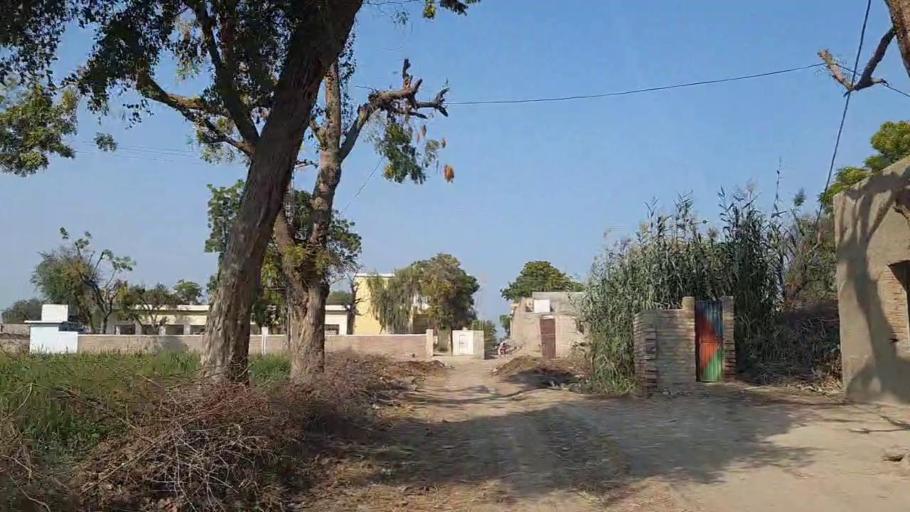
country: PK
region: Sindh
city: Moro
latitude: 26.6848
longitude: 67.9462
